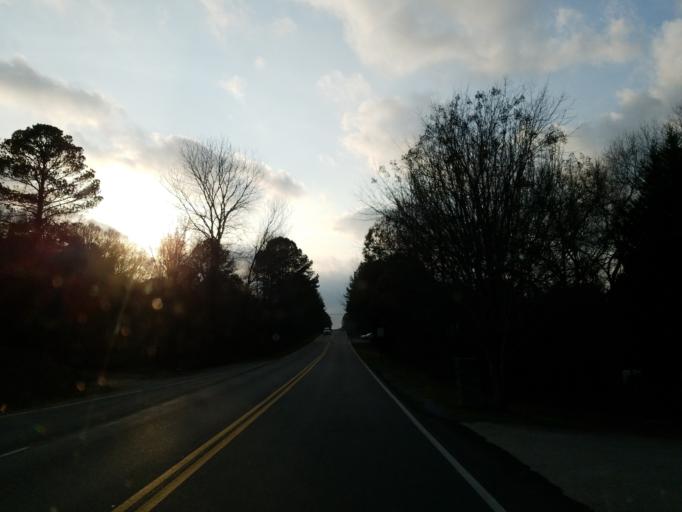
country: US
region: Georgia
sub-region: Bartow County
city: Cartersville
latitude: 34.1172
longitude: -84.8233
